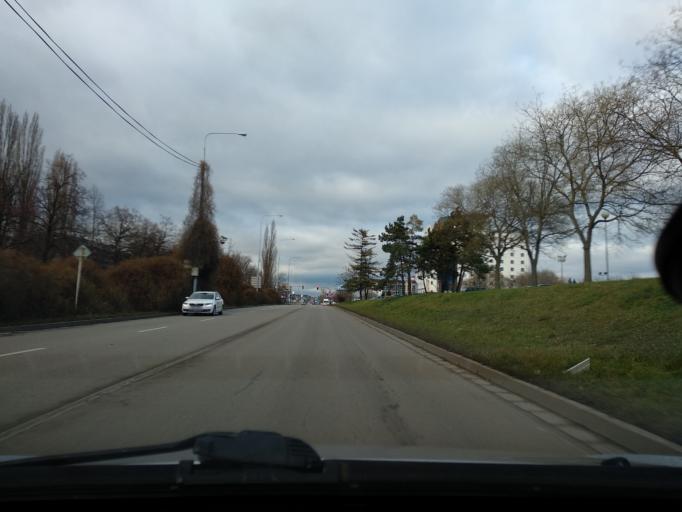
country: CZ
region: South Moravian
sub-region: Mesto Brno
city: Brno
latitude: 49.2103
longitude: 16.6083
